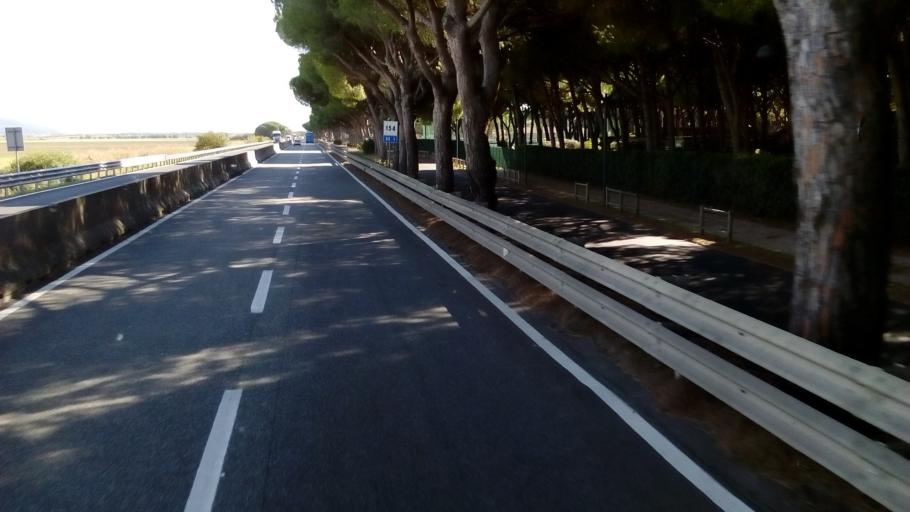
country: IT
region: Tuscany
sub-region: Provincia di Grosseto
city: Fonteblanda
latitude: 42.5313
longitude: 11.1868
